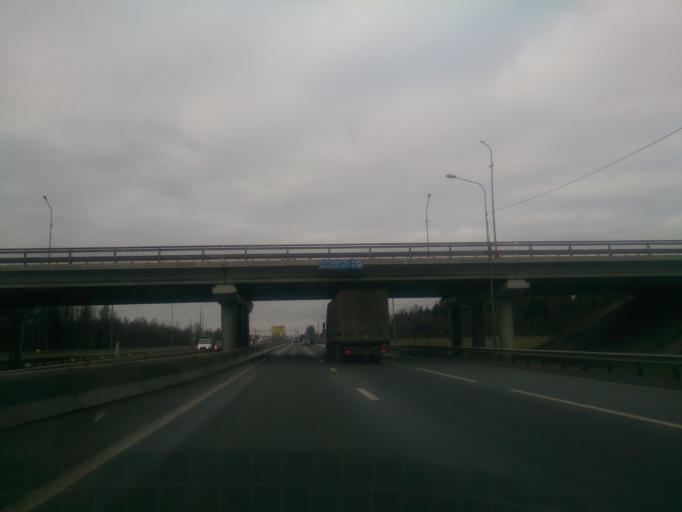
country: RU
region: Leningrad
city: Ul'yanovka
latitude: 59.6053
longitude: 30.7597
